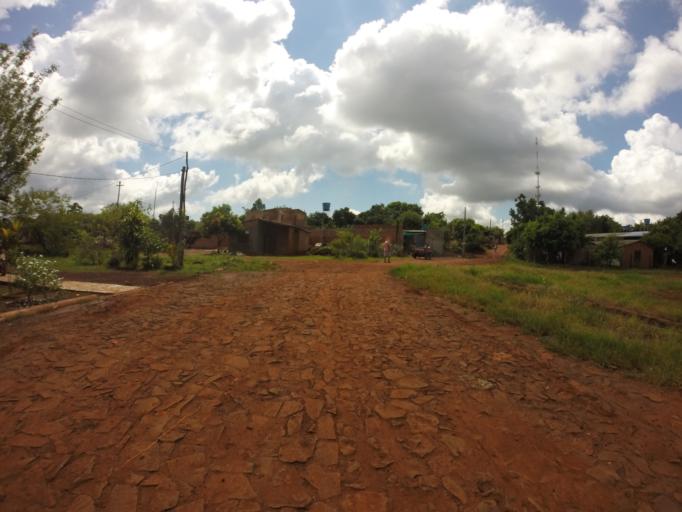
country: PY
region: Alto Parana
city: Ciudad del Este
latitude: -25.4020
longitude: -54.6347
